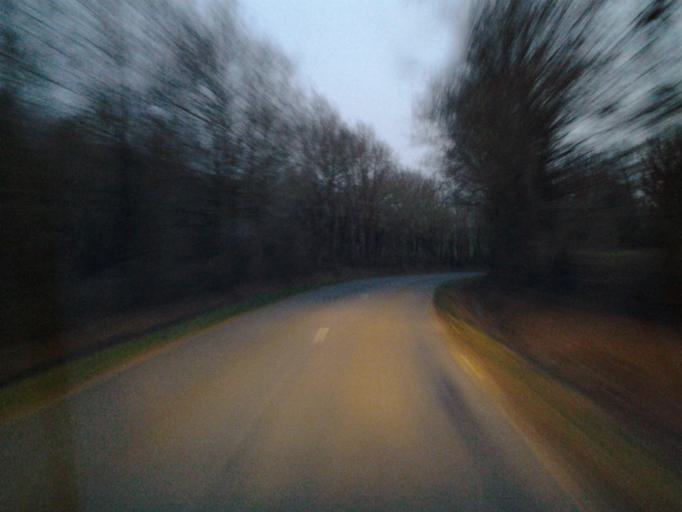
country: FR
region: Pays de la Loire
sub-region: Departement de la Vendee
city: Saint-Florent-des-Bois
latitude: 46.5791
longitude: -1.3544
